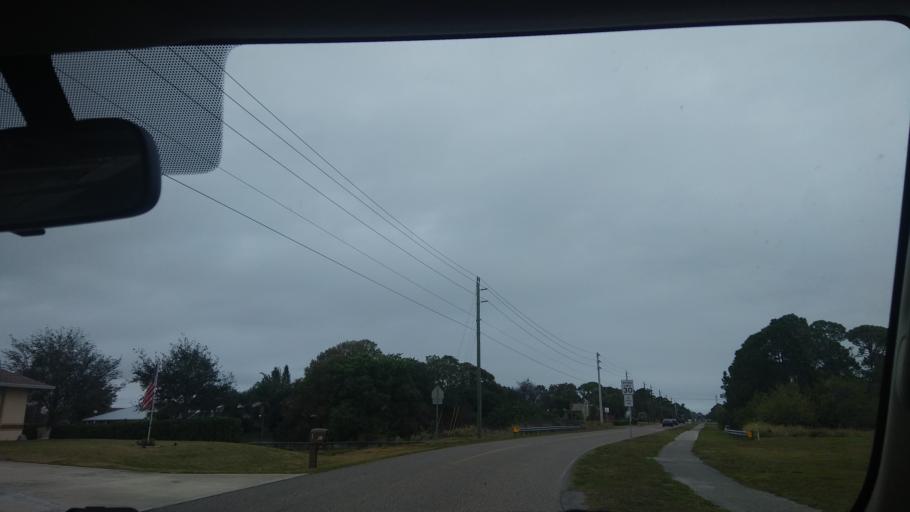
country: US
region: Florida
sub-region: Indian River County
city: Sebastian
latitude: 27.7648
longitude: -80.4659
